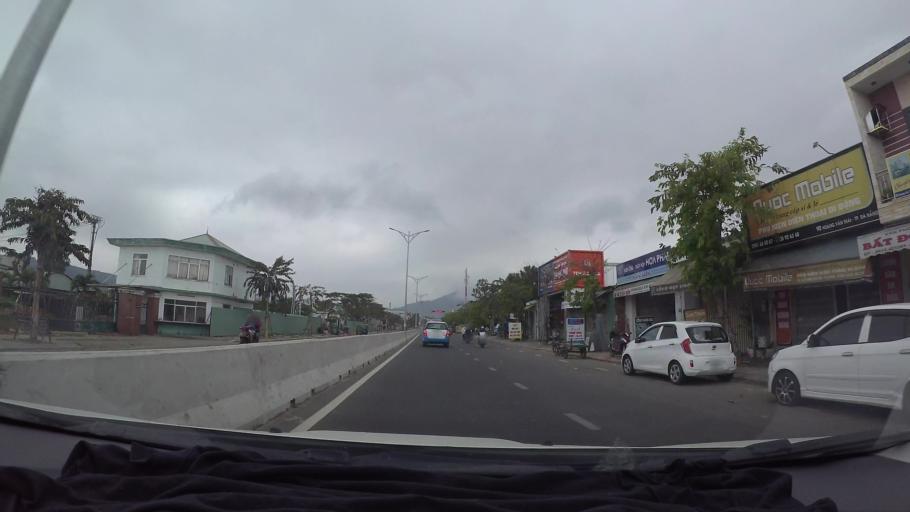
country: VN
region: Da Nang
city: Lien Chieu
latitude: 16.0545
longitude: 108.1602
